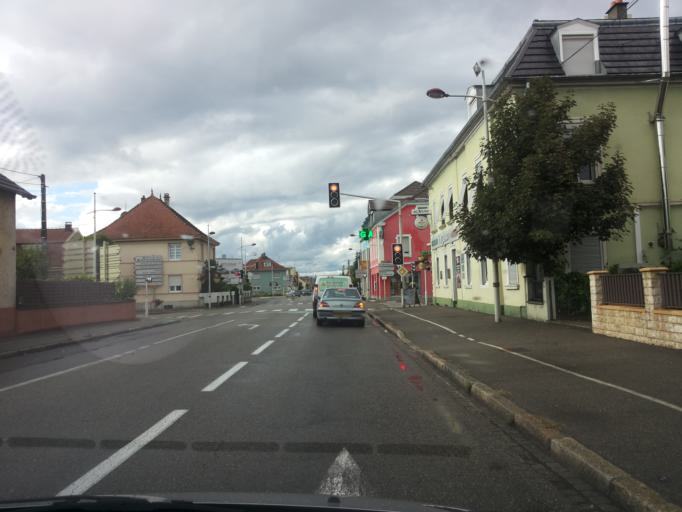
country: FR
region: Alsace
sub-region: Departement du Haut-Rhin
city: Rixheim
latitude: 47.7493
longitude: 7.4076
